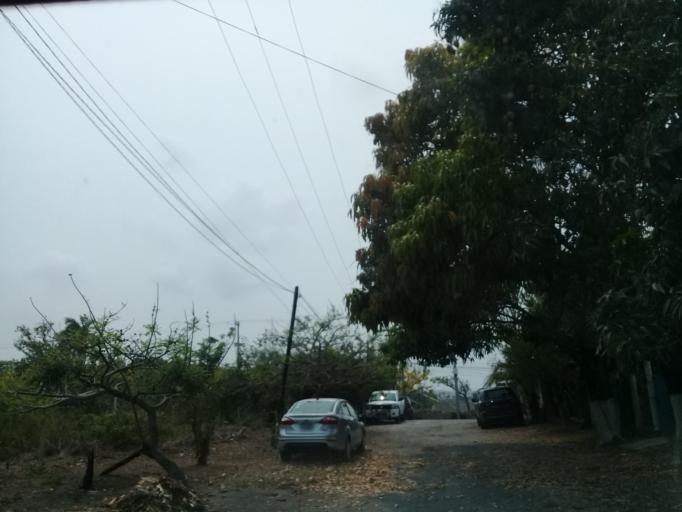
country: MX
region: Veracruz
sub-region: Veracruz
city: Hacienda Sotavento
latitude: 19.1458
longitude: -96.1747
